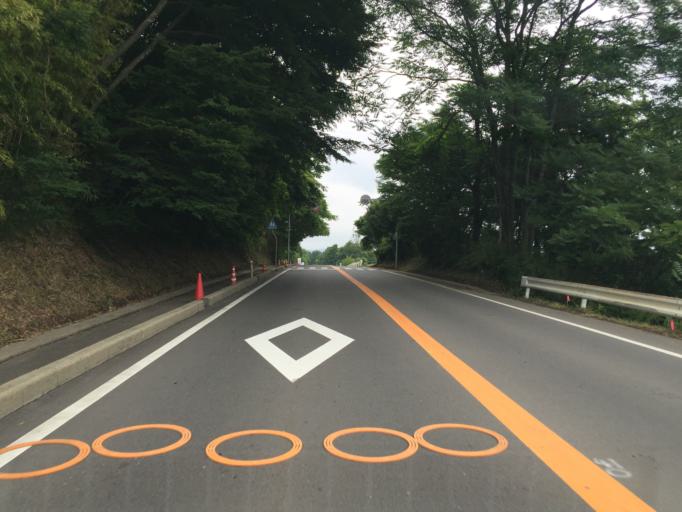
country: JP
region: Fukushima
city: Fukushima-shi
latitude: 37.6854
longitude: 140.5352
